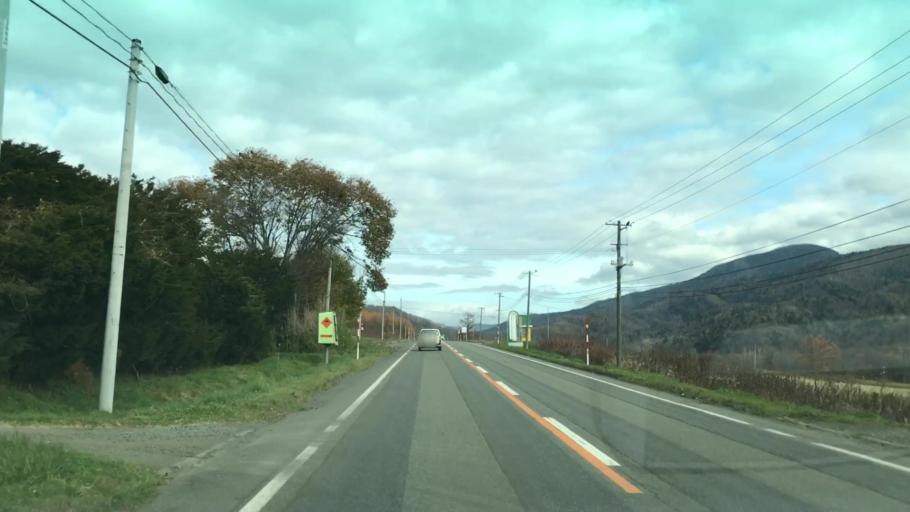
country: JP
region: Hokkaido
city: Shizunai-furukawacho
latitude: 42.7775
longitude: 142.3877
